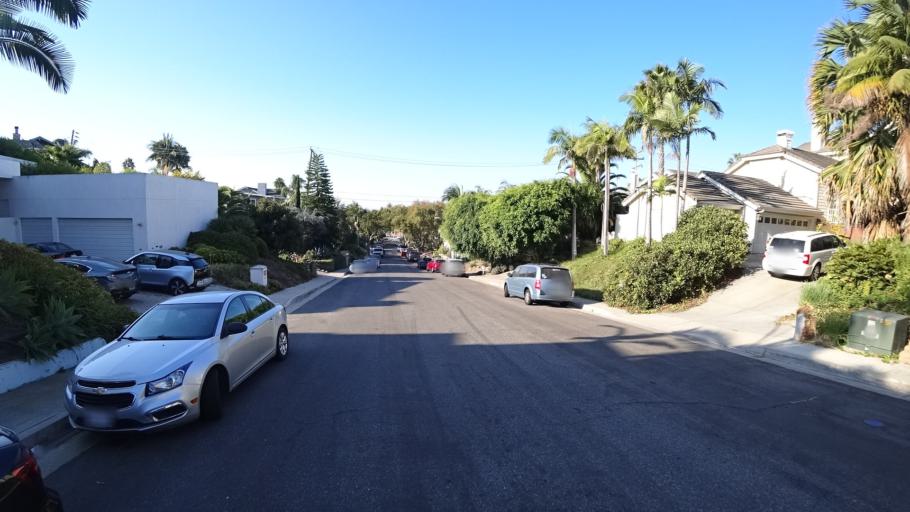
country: US
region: California
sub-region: Orange County
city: San Clemente
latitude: 33.4180
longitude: -117.6006
